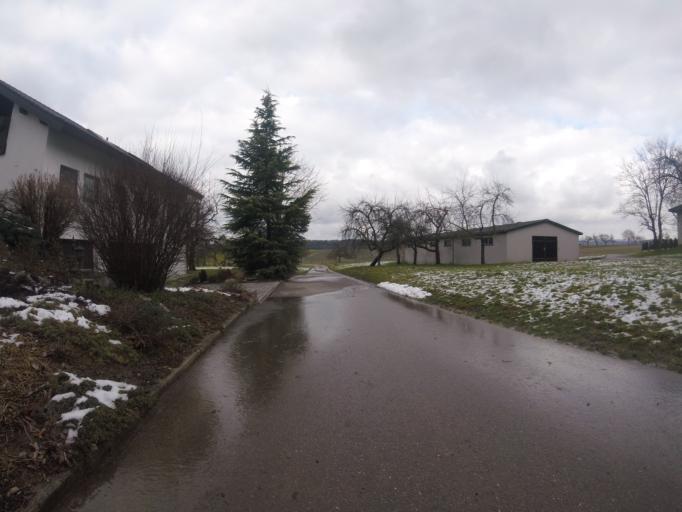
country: DE
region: Baden-Wuerttemberg
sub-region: Regierungsbezirk Stuttgart
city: Aspach
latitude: 48.9658
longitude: 9.3820
